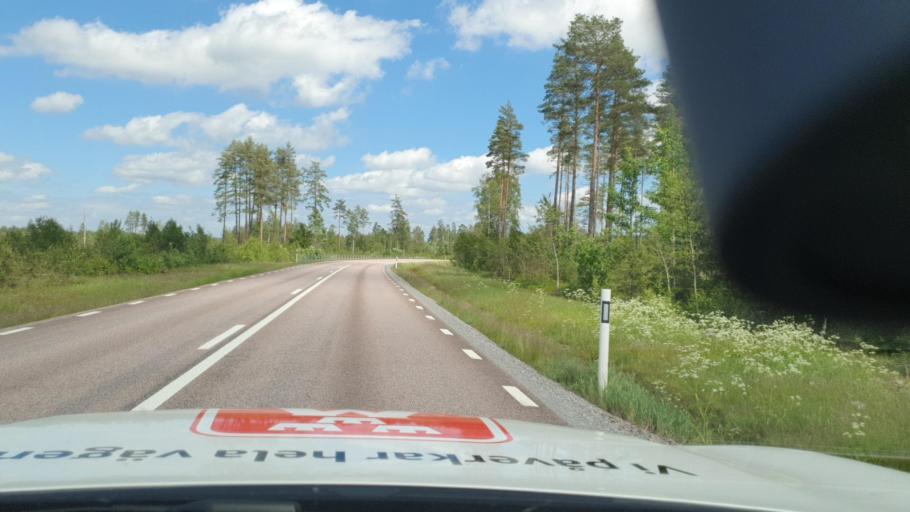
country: SE
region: Vaermland
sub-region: Filipstads Kommun
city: Filipstad
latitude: 59.6530
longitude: 13.9965
